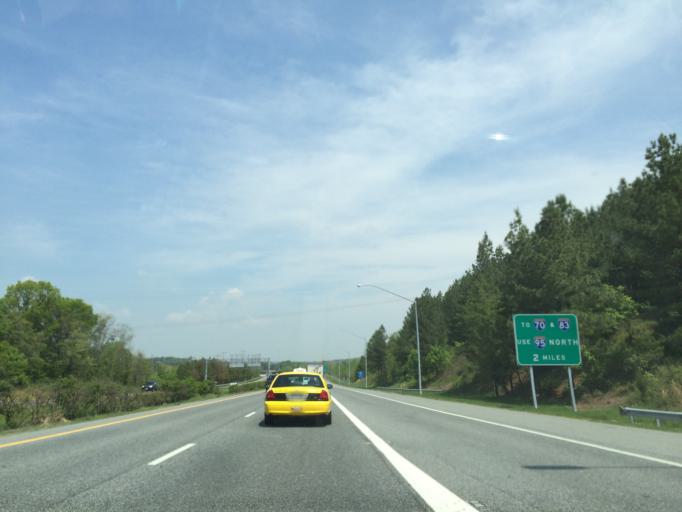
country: US
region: Maryland
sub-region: Howard County
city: Elkridge
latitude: 39.2065
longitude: -76.6954
